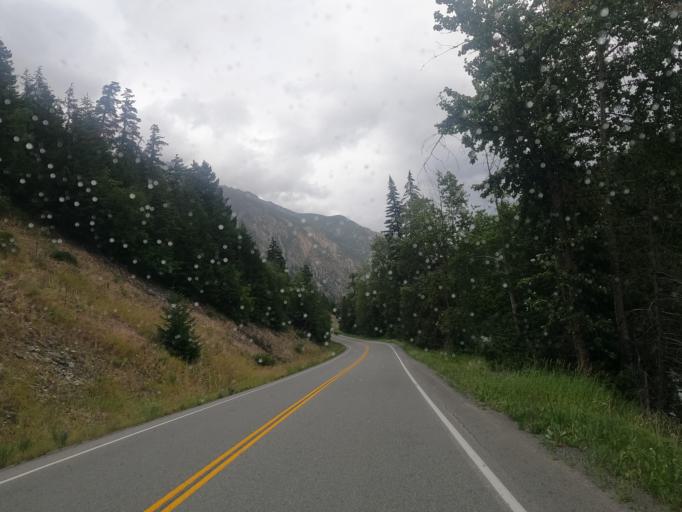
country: CA
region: British Columbia
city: Lillooet
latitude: 50.5214
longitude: -122.1655
